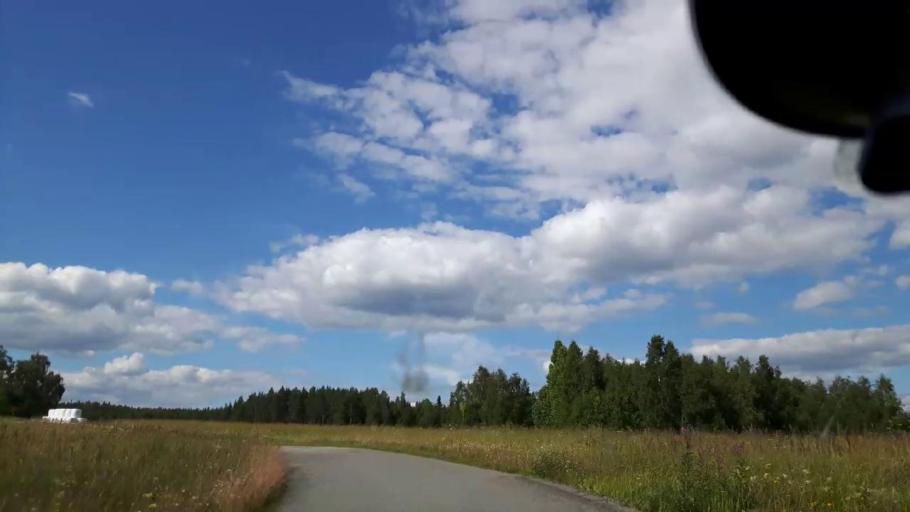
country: SE
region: Jaemtland
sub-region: Braecke Kommun
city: Braecke
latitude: 62.8524
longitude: 15.2944
